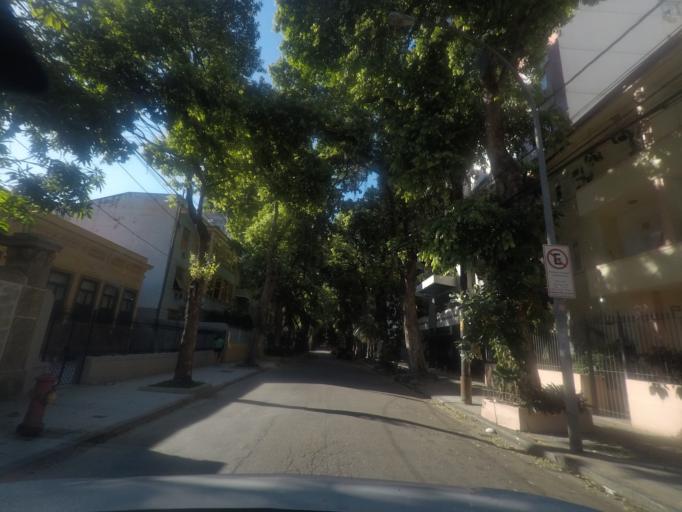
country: BR
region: Rio de Janeiro
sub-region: Rio De Janeiro
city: Rio de Janeiro
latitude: -22.9502
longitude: -43.1895
